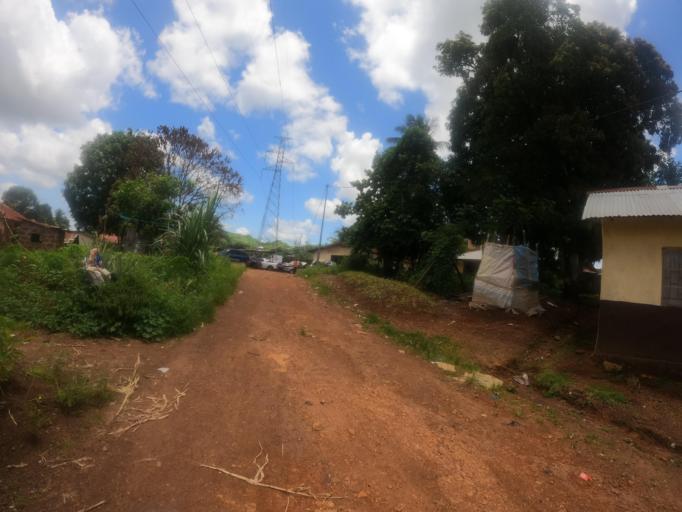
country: SL
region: Northern Province
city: Makeni
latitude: 8.8868
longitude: -12.0717
